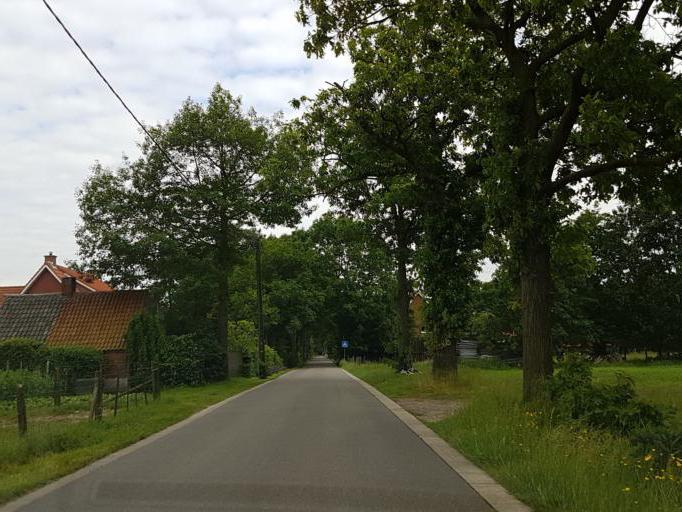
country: BE
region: Flanders
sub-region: Provincie Antwerpen
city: Zoersel
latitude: 51.2750
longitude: 4.6804
